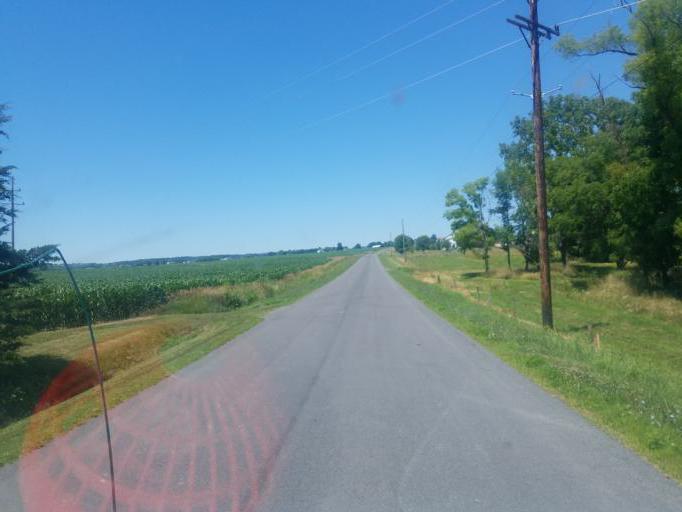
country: US
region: New York
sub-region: Yates County
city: Penn Yan
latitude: 42.6641
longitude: -77.0197
